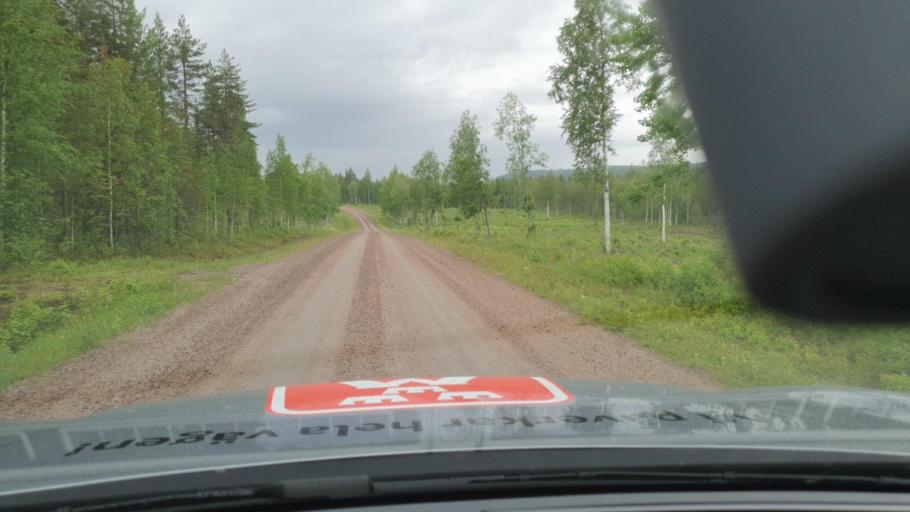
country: SE
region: Norrbotten
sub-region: Overkalix Kommun
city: OEverkalix
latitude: 66.6038
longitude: 22.7475
